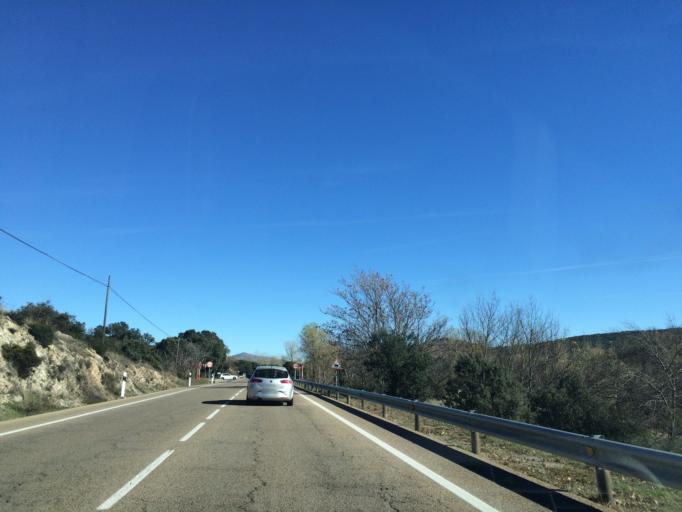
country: ES
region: Madrid
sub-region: Provincia de Madrid
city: Boalo
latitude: 40.7152
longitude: -3.8958
